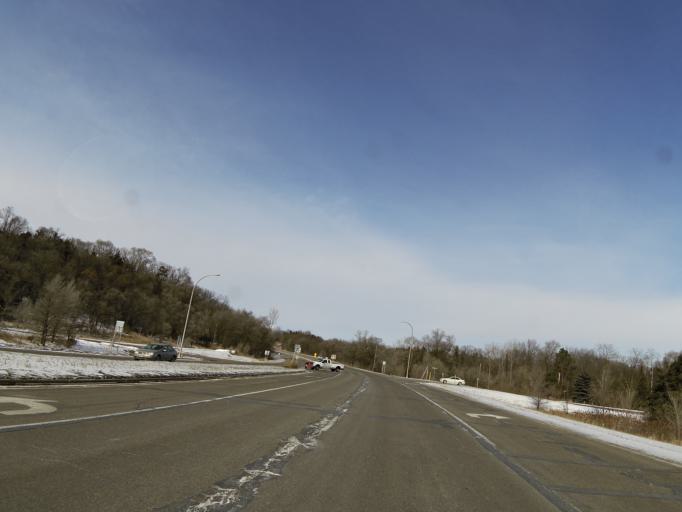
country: US
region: Minnesota
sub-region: Washington County
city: Lakeland
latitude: 44.9648
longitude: -92.7723
